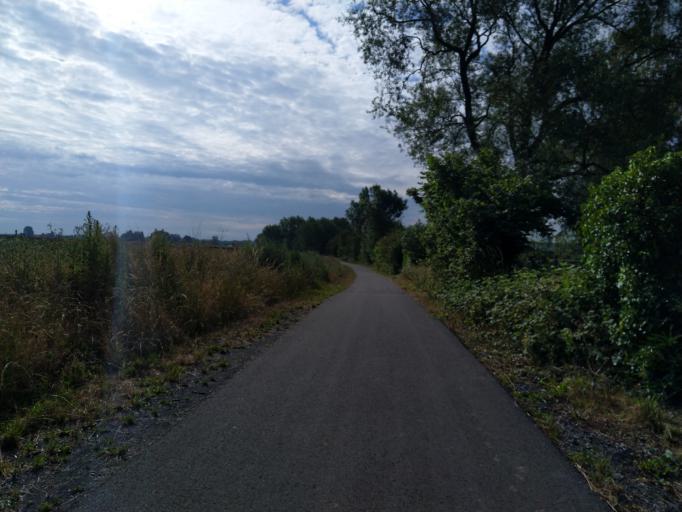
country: BE
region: Wallonia
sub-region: Province du Hainaut
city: Erquelinnes
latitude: 50.3159
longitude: 4.1066
